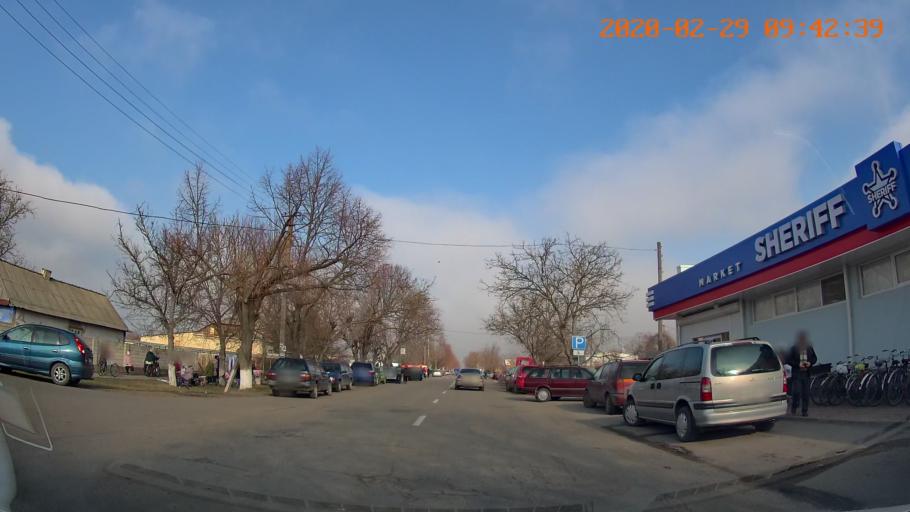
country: MD
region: Telenesti
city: Crasnoe
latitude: 46.6416
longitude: 29.8236
